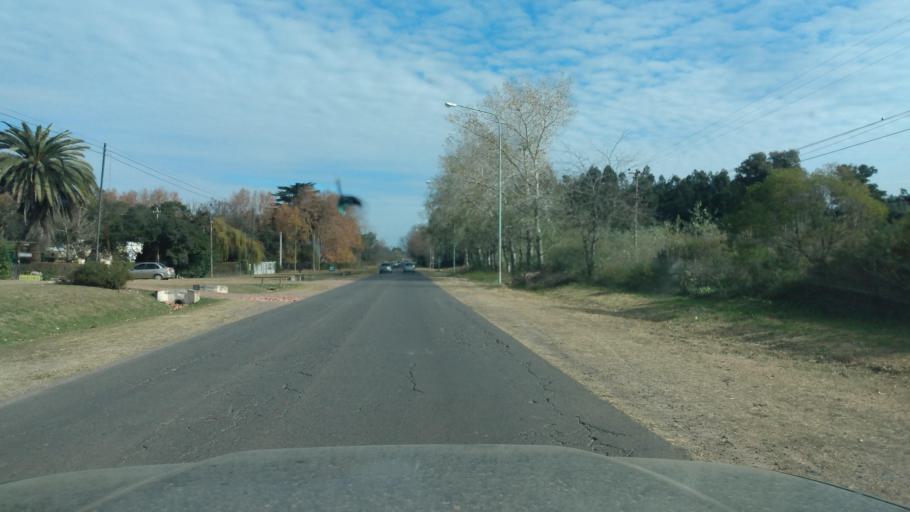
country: AR
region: Buenos Aires
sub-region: Partido de Lujan
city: Lujan
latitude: -34.5719
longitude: -59.1563
